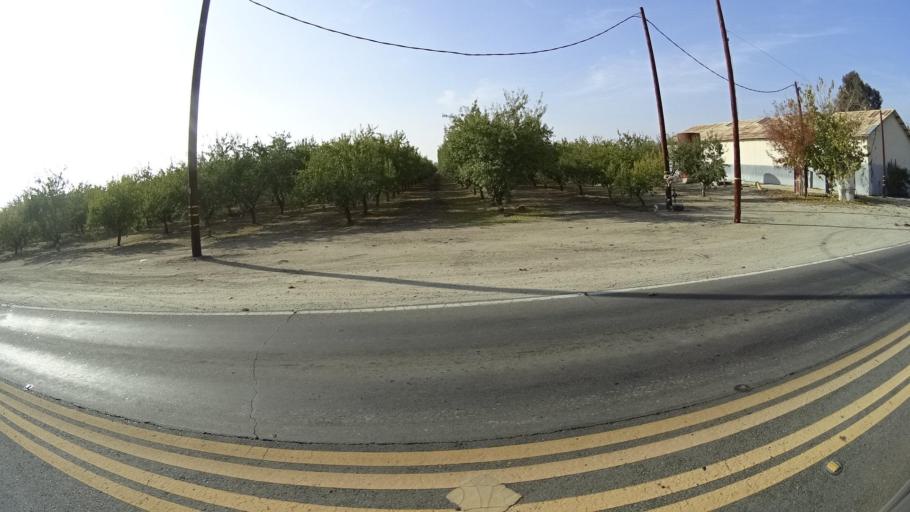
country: US
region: California
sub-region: Kern County
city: Delano
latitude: 35.7596
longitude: -119.2232
